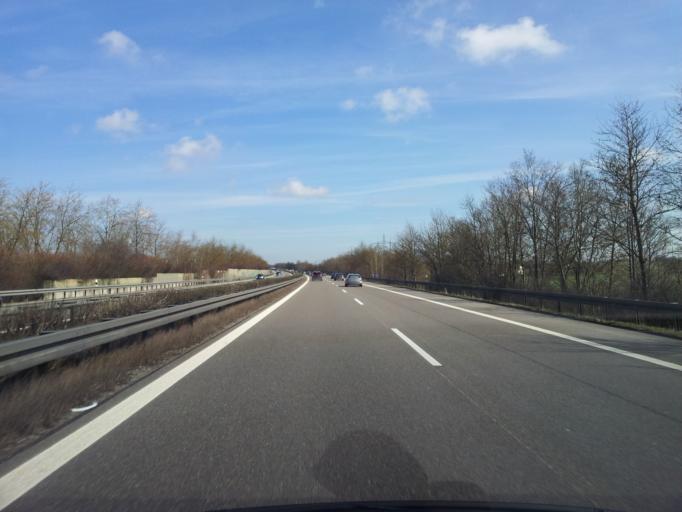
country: DE
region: Baden-Wuerttemberg
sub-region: Regierungsbezirk Stuttgart
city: Motzingen
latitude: 48.4603
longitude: 8.7801
